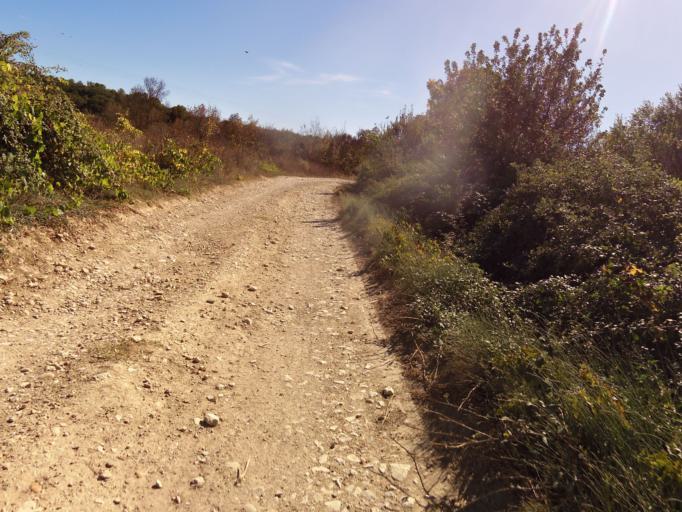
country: FR
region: Languedoc-Roussillon
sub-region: Departement du Gard
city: Vergeze
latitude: 43.7598
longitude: 4.2135
